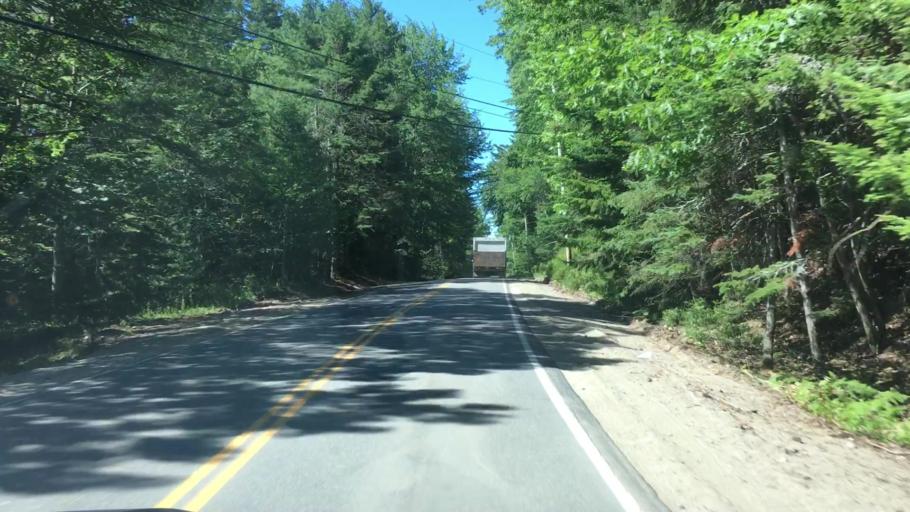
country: US
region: Maine
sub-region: Hancock County
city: Sedgwick
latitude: 44.3670
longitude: -68.5682
